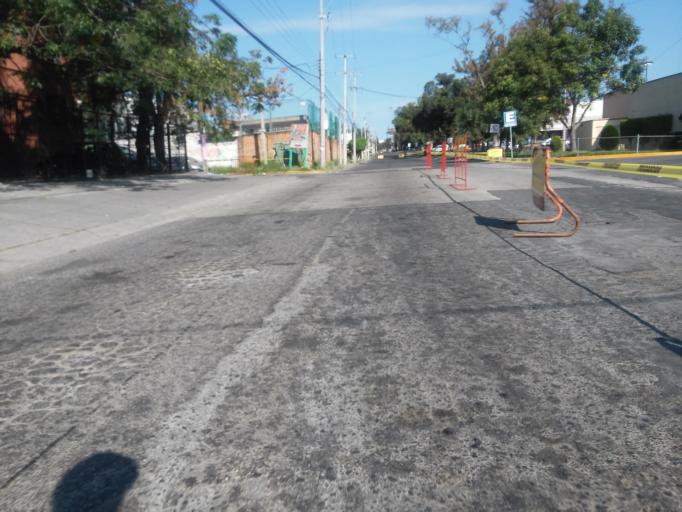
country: MX
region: Jalisco
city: Guadalajara
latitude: 20.6409
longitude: -103.4156
